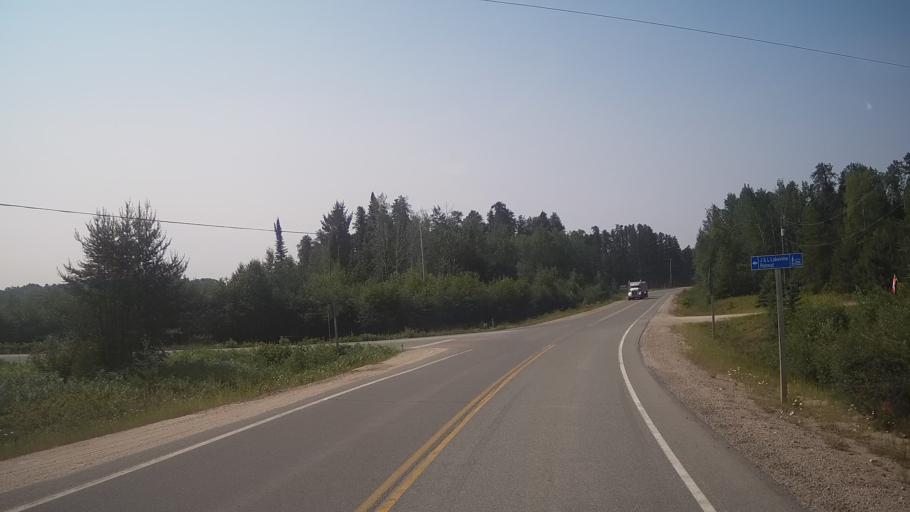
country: CA
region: Ontario
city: Timmins
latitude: 47.6805
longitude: -81.7157
